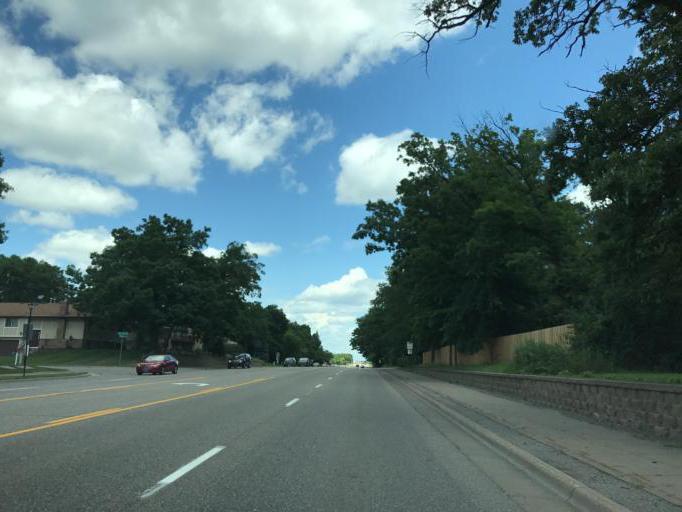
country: US
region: Minnesota
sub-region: Hennepin County
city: Maple Grove
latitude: 45.0738
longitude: -93.4311
